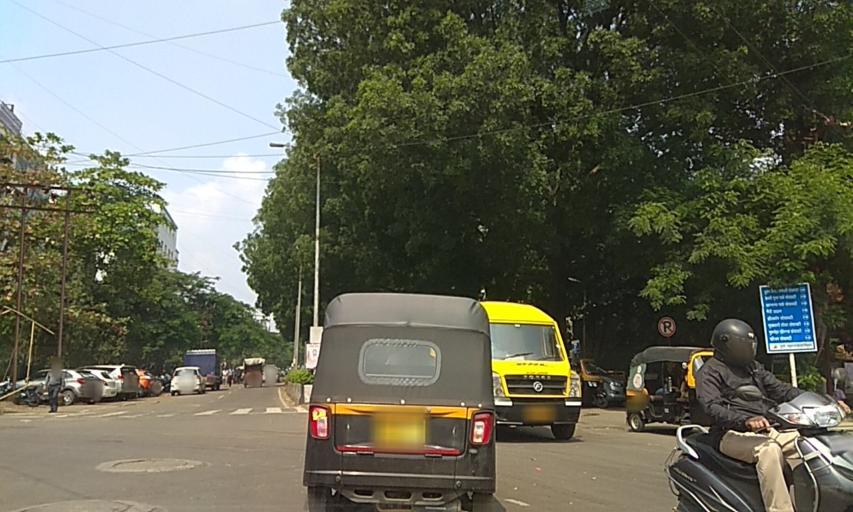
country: IN
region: Maharashtra
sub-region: Pune Division
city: Lohogaon
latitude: 18.5650
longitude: 73.9182
